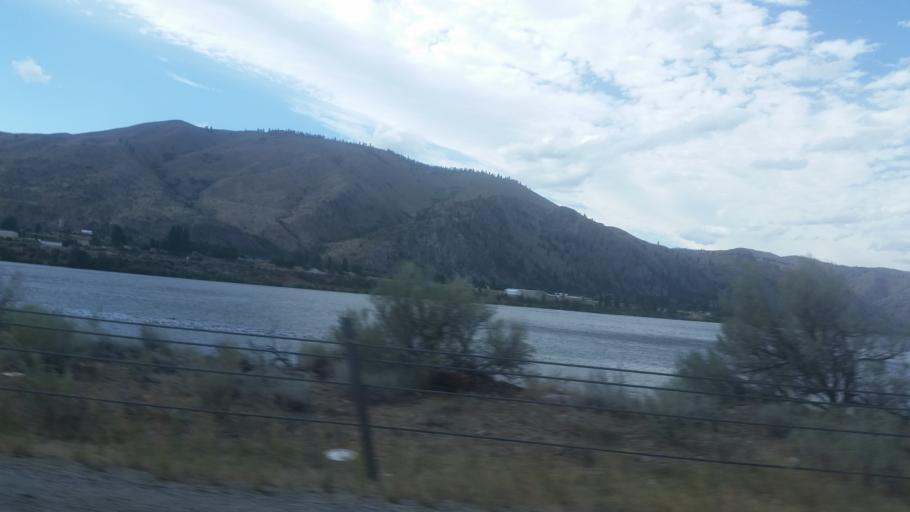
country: US
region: Washington
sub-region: Chelan County
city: Entiat
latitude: 47.6824
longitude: -120.1937
